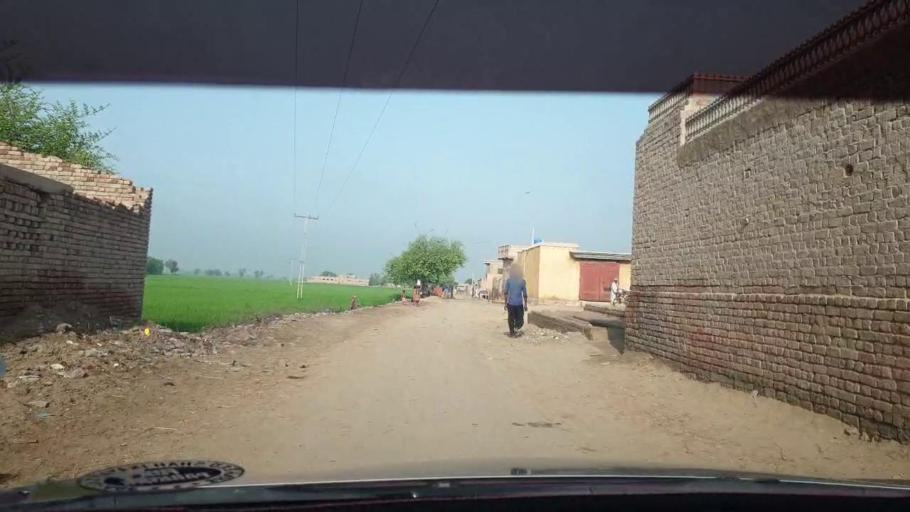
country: PK
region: Sindh
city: Goth Garelo
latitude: 27.4838
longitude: 68.0337
